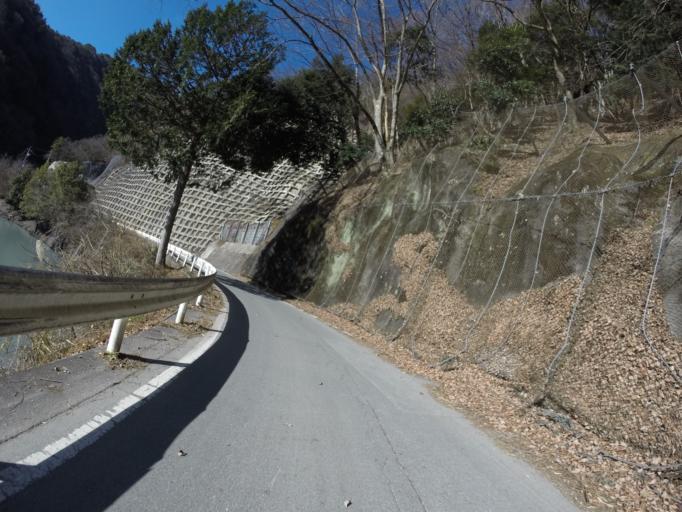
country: JP
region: Yamanashi
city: Ryuo
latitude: 35.4100
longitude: 138.3300
